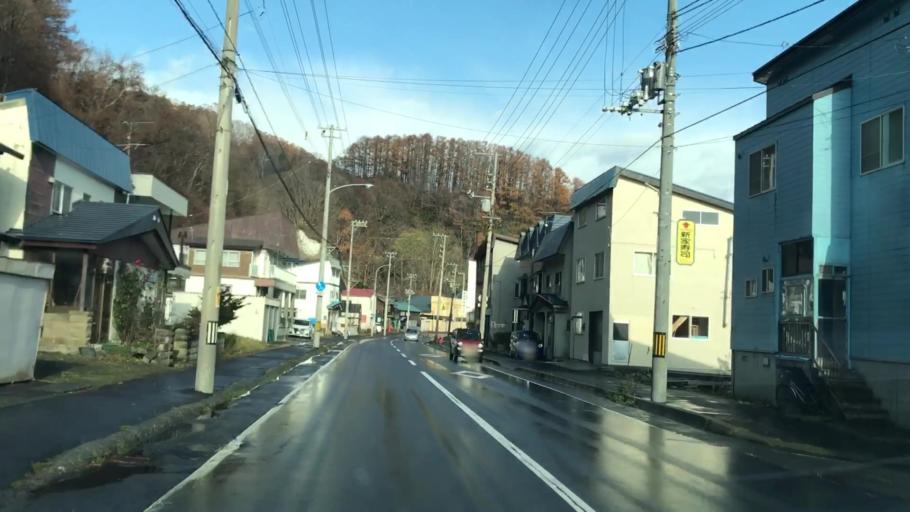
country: JP
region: Hokkaido
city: Yoichi
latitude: 43.2728
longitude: 140.6359
